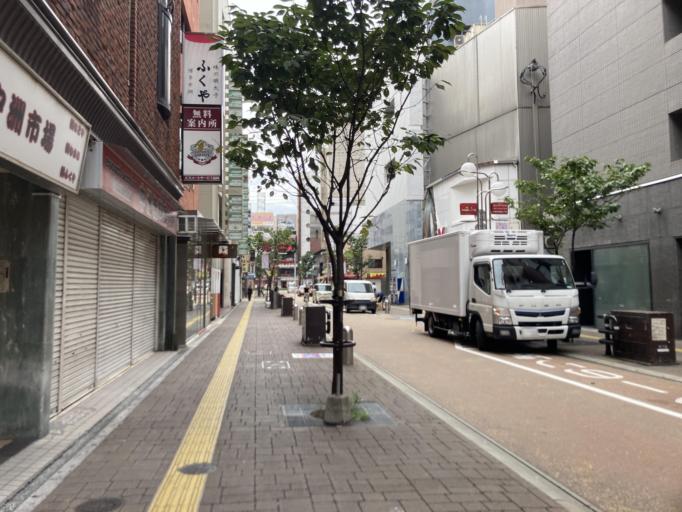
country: JP
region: Fukuoka
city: Fukuoka-shi
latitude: 33.5922
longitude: 130.4079
